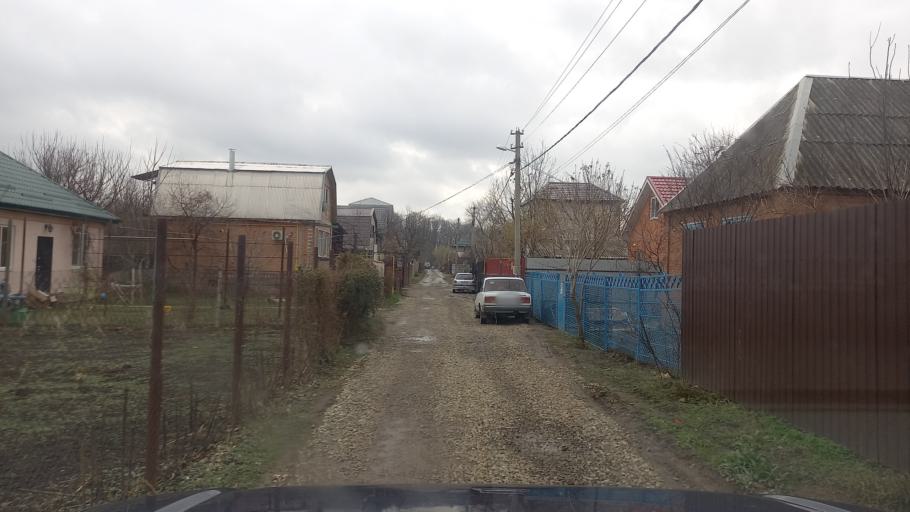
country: RU
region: Krasnodarskiy
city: Pashkovskiy
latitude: 45.0552
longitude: 39.1780
